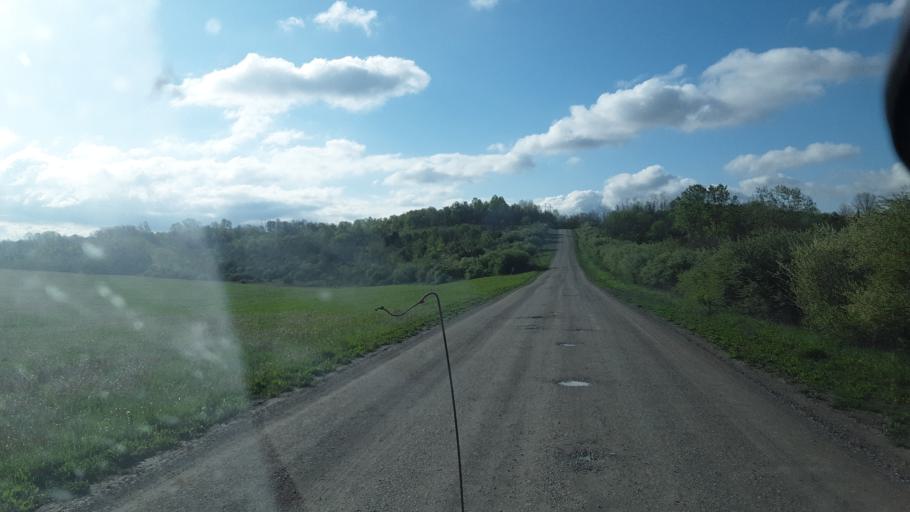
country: US
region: Ohio
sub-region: Noble County
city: Caldwell
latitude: 39.7986
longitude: -81.6336
